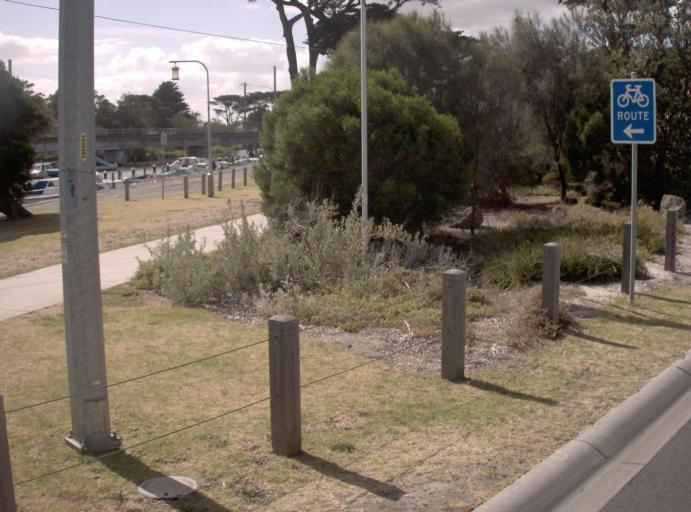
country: AU
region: Victoria
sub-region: Kingston
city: Mordialloc
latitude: -38.0096
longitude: 145.0884
